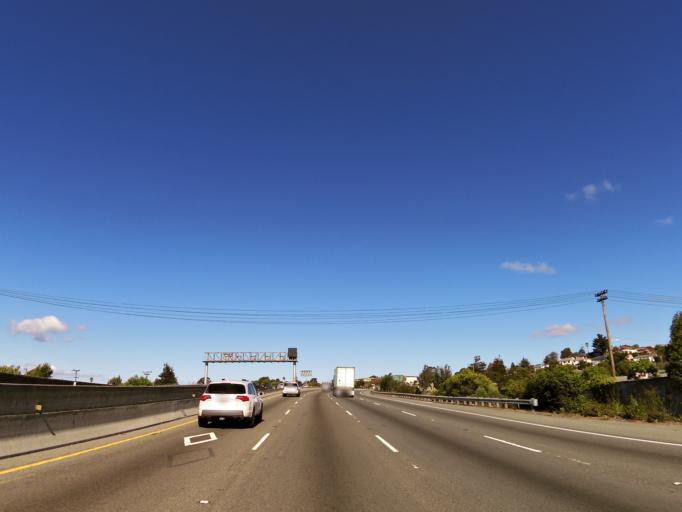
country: US
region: California
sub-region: Contra Costa County
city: El Cerrito
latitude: 37.9086
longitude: -122.3161
